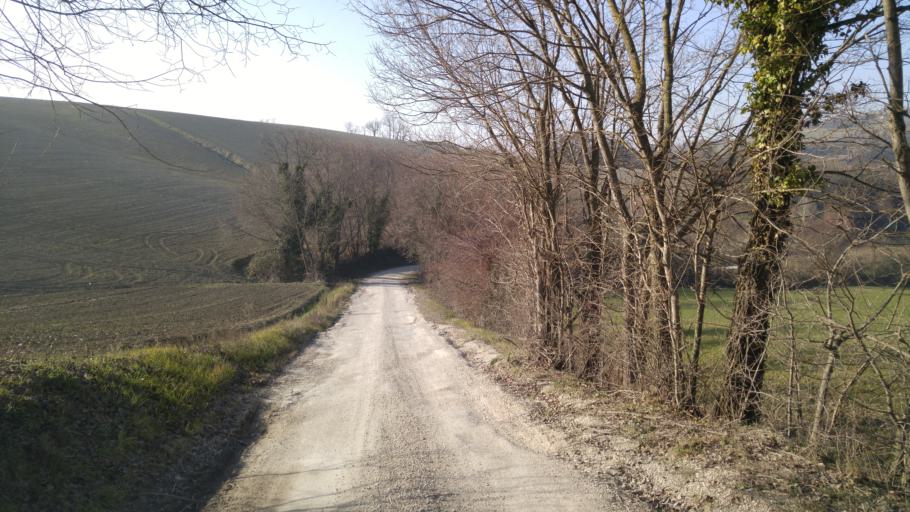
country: IT
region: The Marches
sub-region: Provincia di Pesaro e Urbino
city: Cuccurano
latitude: 43.8128
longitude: 12.9346
